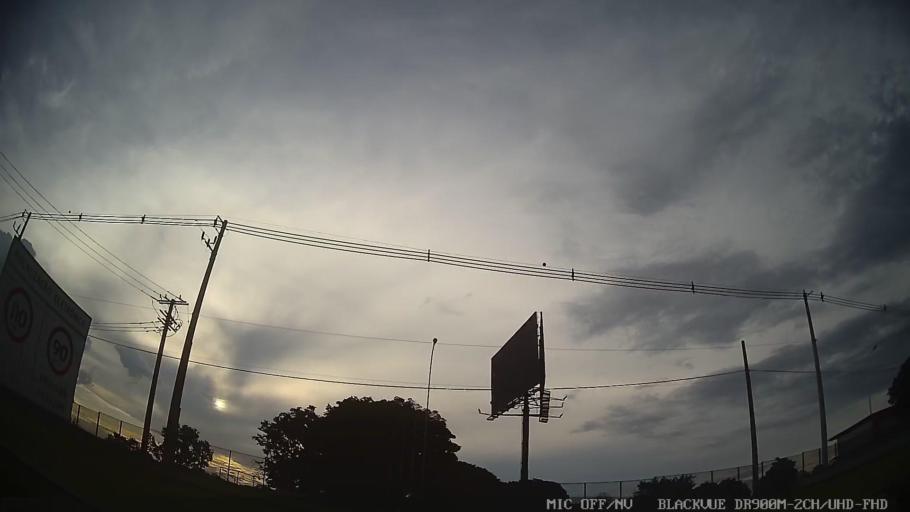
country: BR
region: Sao Paulo
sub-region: Jaguariuna
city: Jaguariuna
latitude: -22.6916
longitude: -47.0128
